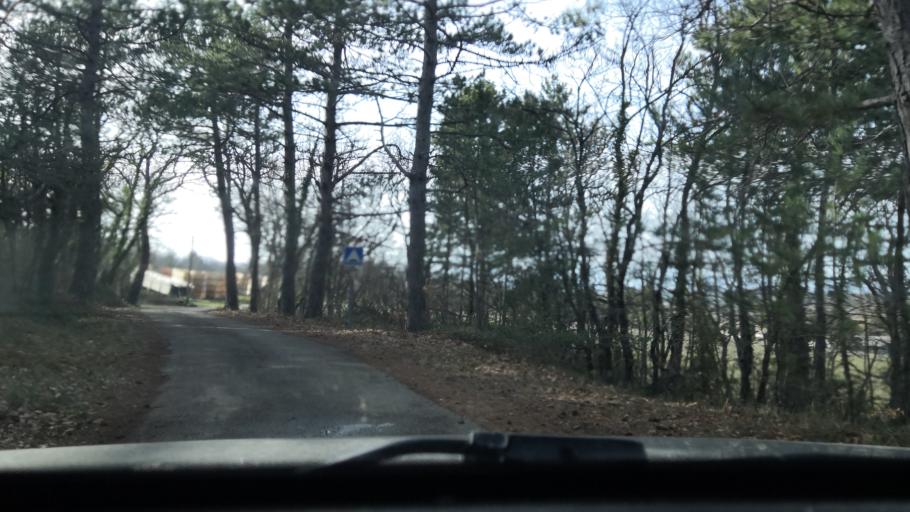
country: FR
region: Rhone-Alpes
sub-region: Departement de la Drome
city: La Begude-de-Mazenc
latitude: 44.5379
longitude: 4.9462
